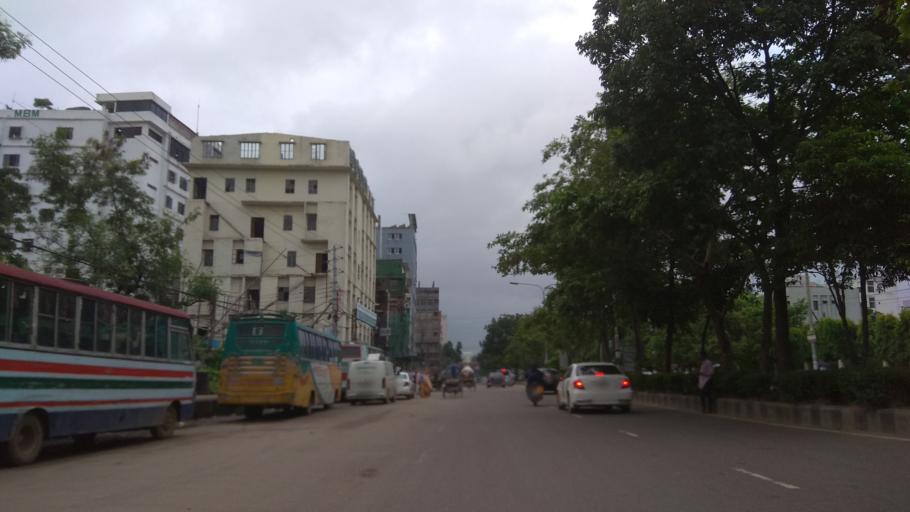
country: BD
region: Dhaka
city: Azimpur
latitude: 23.8023
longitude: 90.3794
